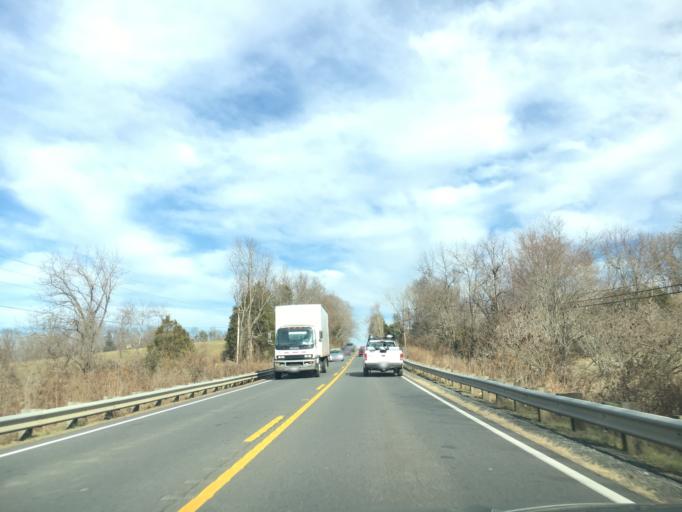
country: US
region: Virginia
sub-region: Culpeper County
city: Culpeper
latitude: 38.6157
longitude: -77.9475
